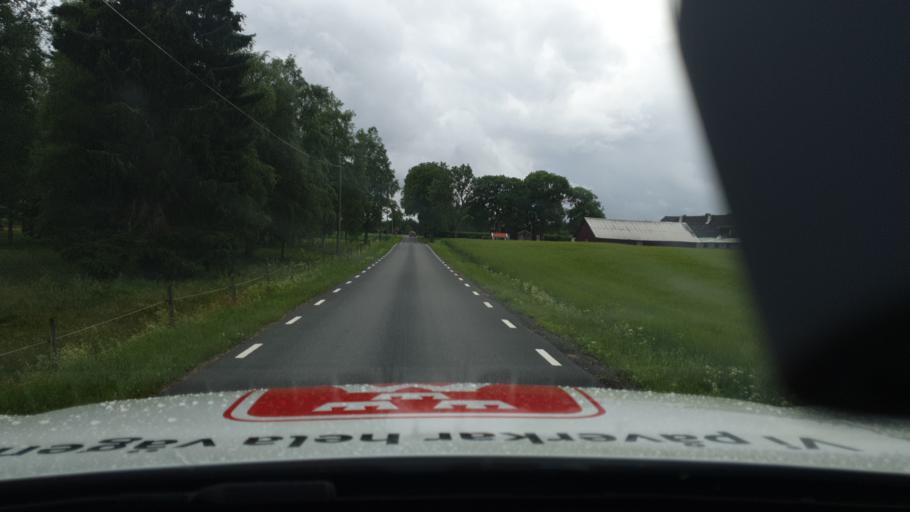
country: SE
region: Joenkoeping
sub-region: Mullsjo Kommun
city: Mullsjoe
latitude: 57.9642
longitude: 13.7380
